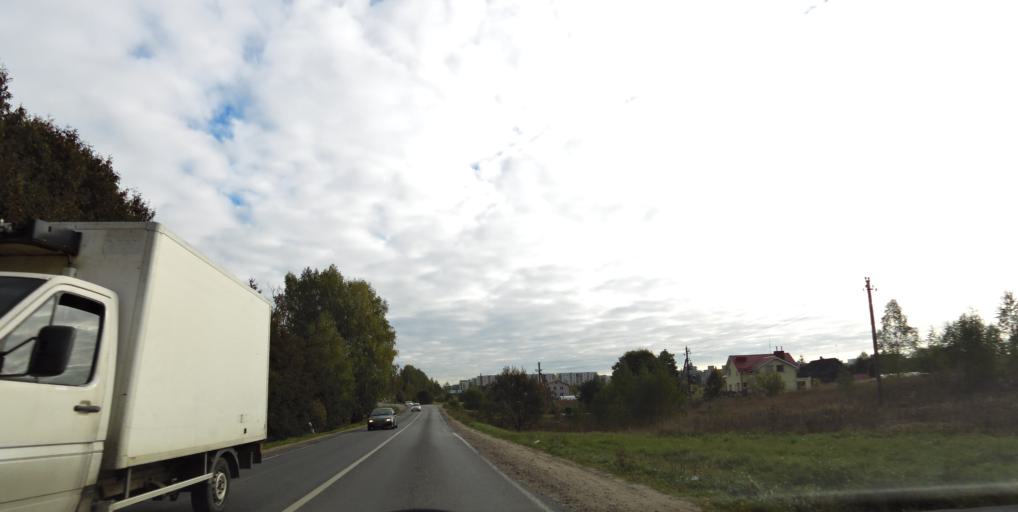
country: LT
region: Vilnius County
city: Pilaite
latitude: 54.7105
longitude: 25.1651
